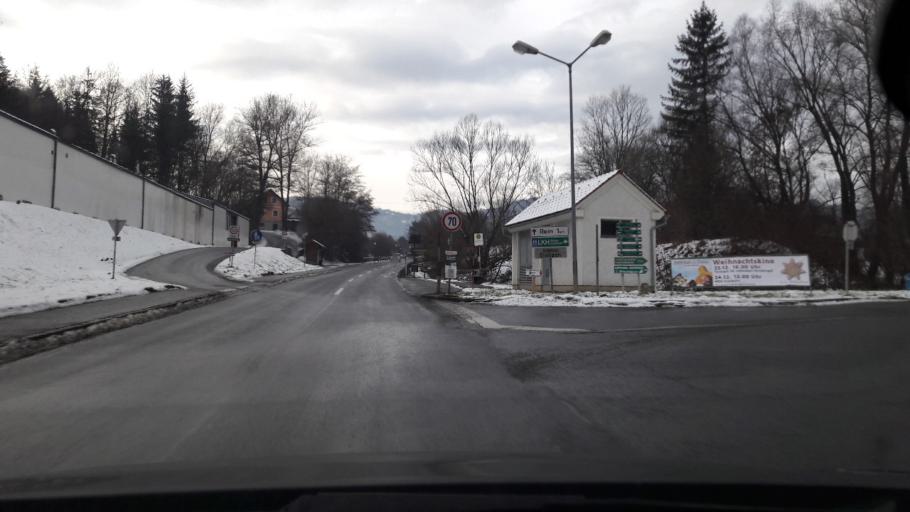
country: AT
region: Styria
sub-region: Politischer Bezirk Graz-Umgebung
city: Gratwein
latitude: 47.1321
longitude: 15.3081
